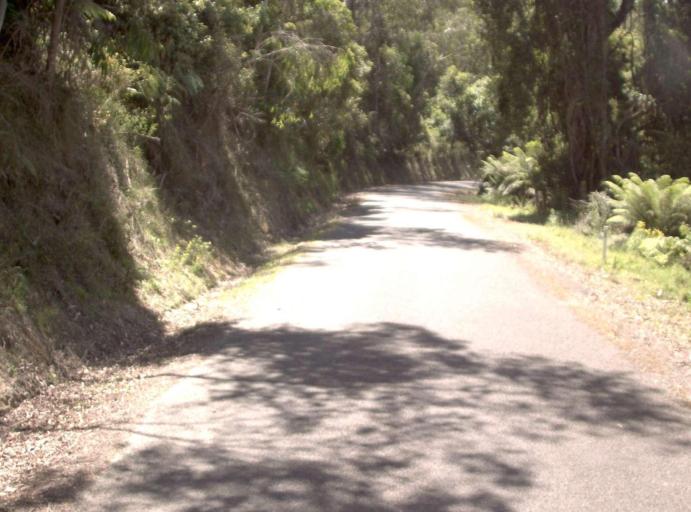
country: AU
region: New South Wales
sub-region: Bombala
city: Bombala
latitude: -37.4549
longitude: 148.9305
